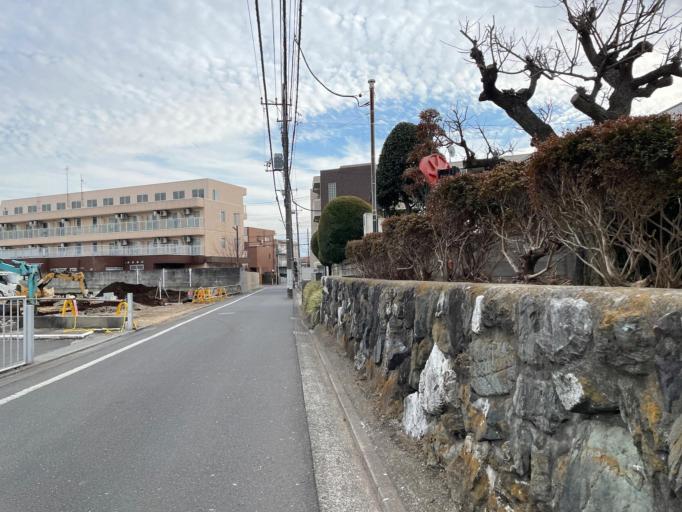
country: JP
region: Tokyo
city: Kamirenjaku
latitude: 35.7052
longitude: 139.5396
